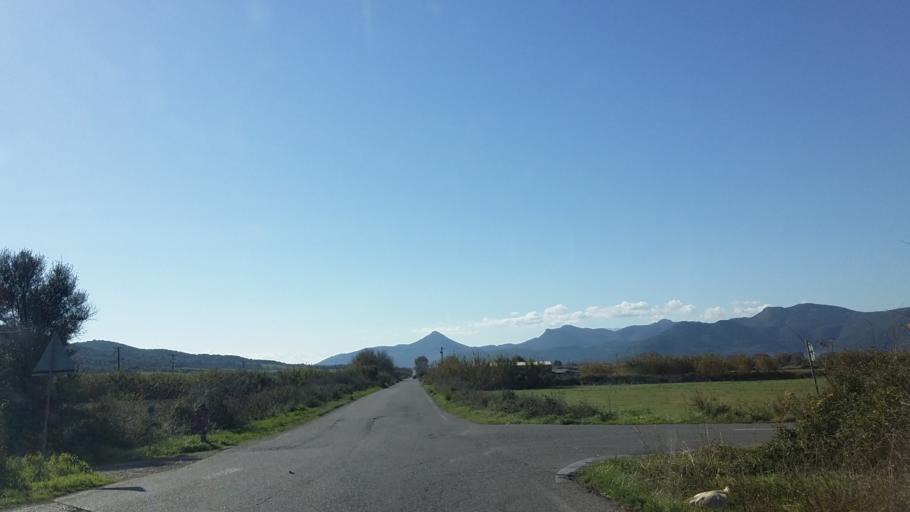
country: GR
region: West Greece
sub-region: Nomos Aitolias kai Akarnanias
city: Vonitsa
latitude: 38.8675
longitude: 20.8839
